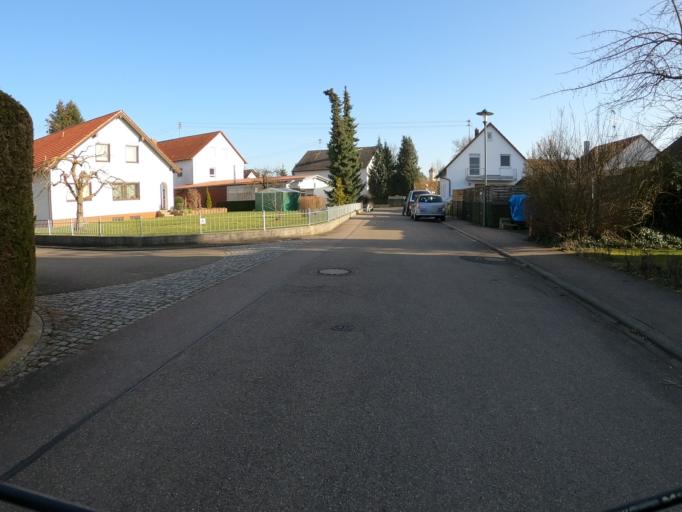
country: DE
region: Bavaria
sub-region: Swabia
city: Nersingen
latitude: 48.4173
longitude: 10.1331
